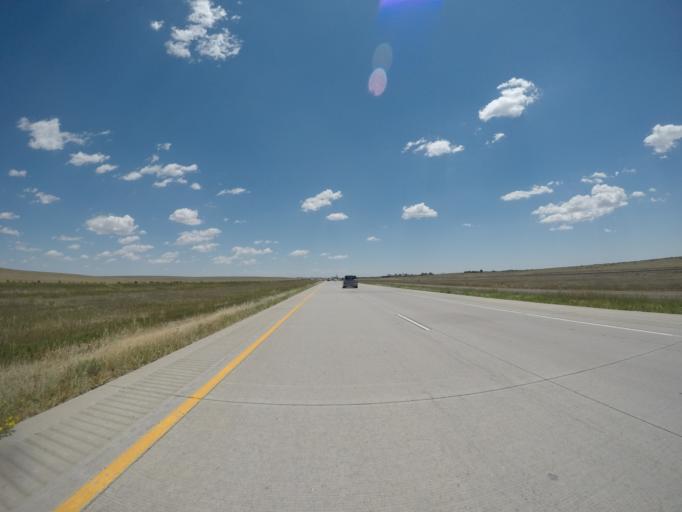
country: US
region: Colorado
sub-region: Lincoln County
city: Limon
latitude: 39.2779
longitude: -103.7563
